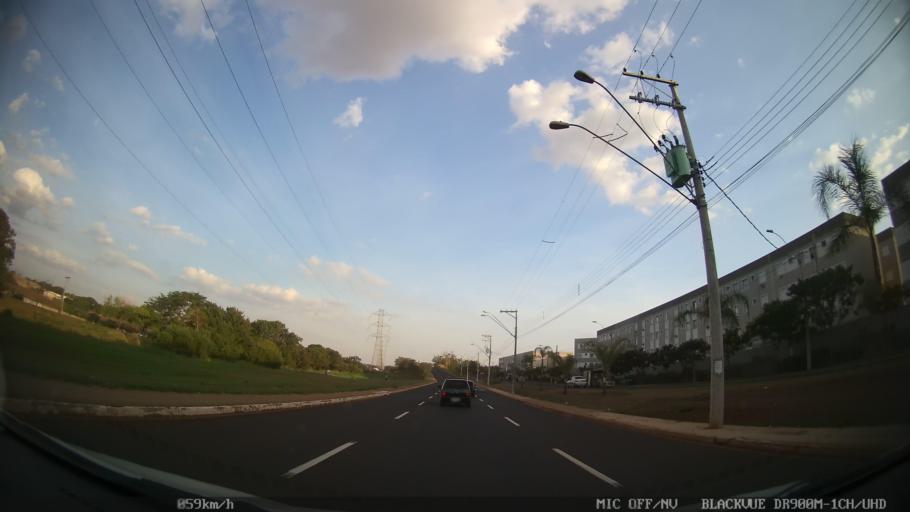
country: BR
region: Sao Paulo
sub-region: Ribeirao Preto
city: Ribeirao Preto
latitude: -21.1337
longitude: -47.8042
